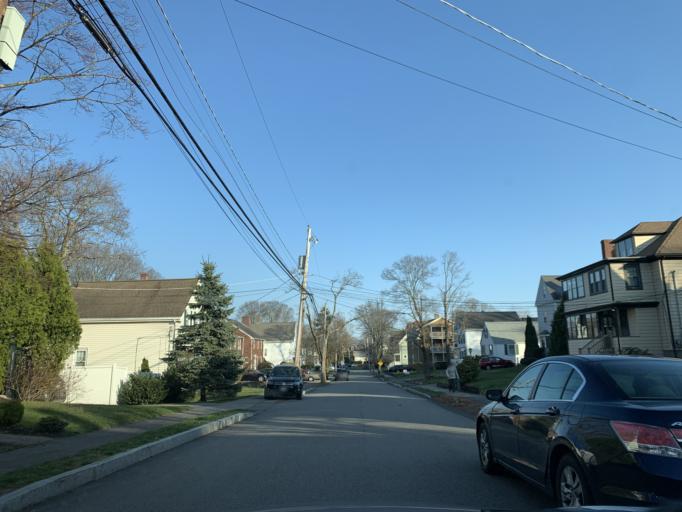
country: US
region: Massachusetts
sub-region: Norfolk County
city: Norwood
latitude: 42.1957
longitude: -71.2072
